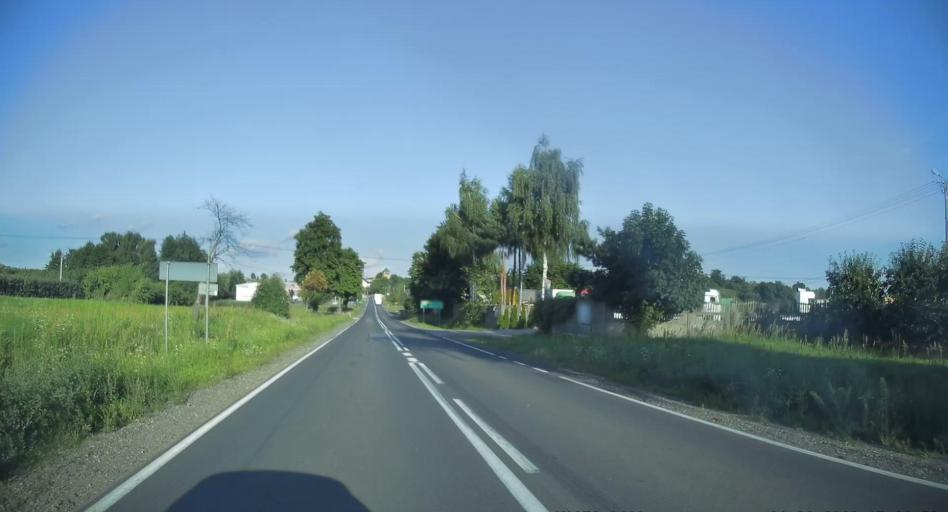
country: PL
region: Masovian Voivodeship
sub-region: Powiat grojecki
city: Bledow
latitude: 51.8013
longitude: 20.6144
